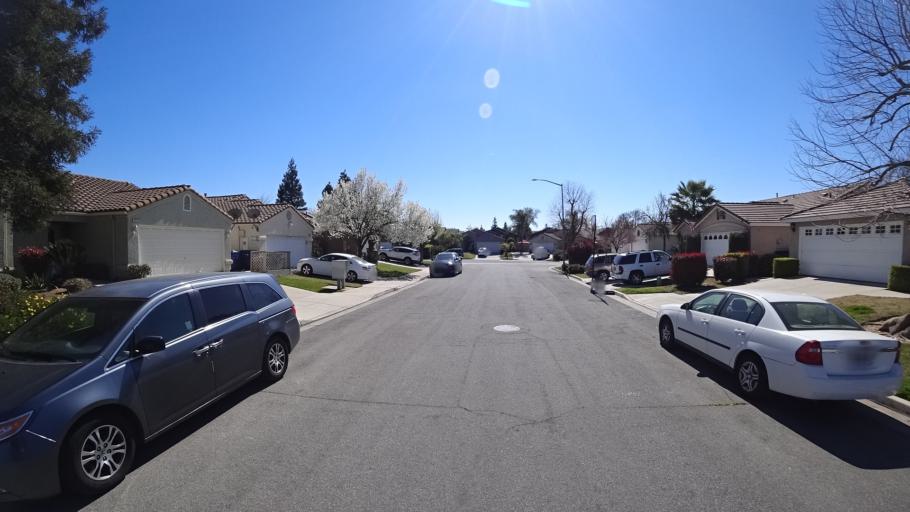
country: US
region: California
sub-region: Fresno County
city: Clovis
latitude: 36.8430
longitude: -119.7518
